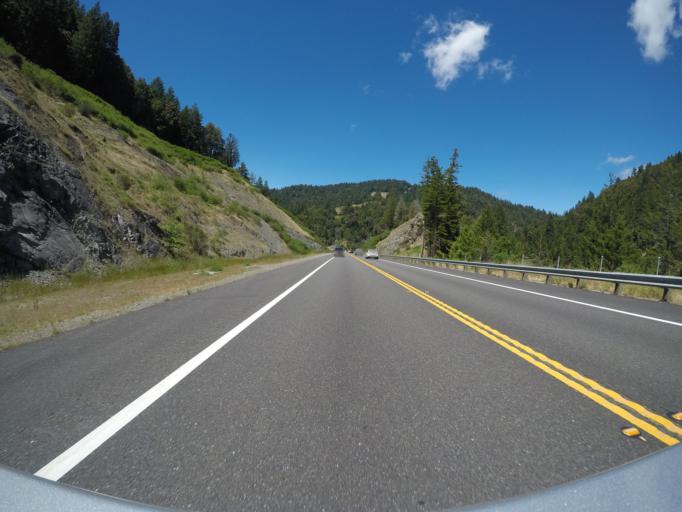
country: US
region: California
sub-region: Humboldt County
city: Redway
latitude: 39.9242
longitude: -123.7612
